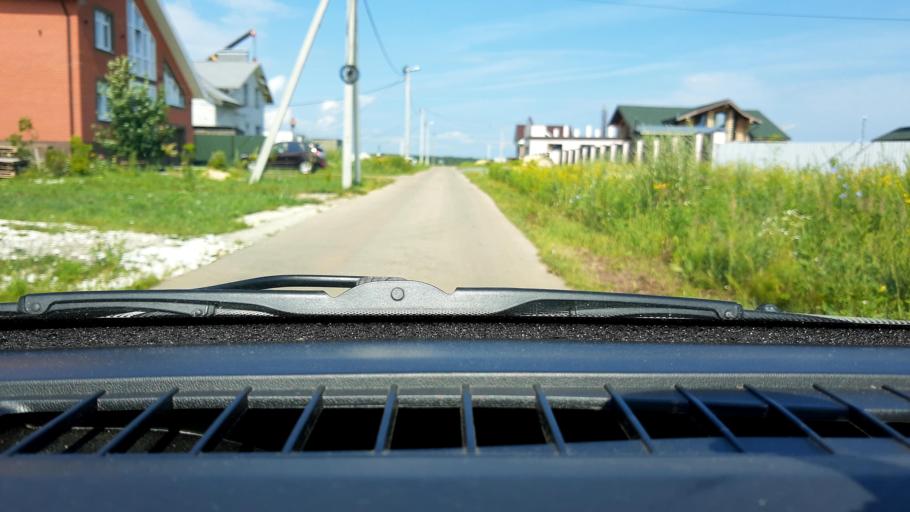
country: RU
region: Nizjnij Novgorod
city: Burevestnik
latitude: 56.1470
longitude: 43.7281
